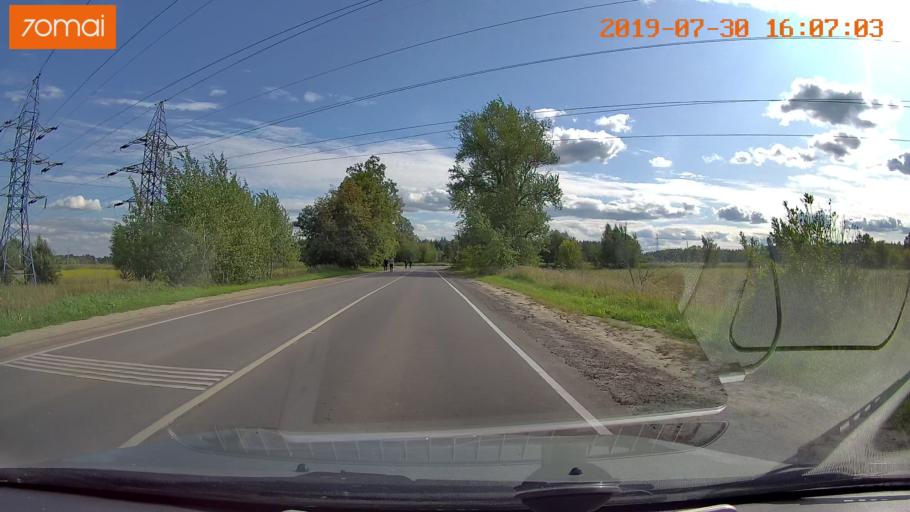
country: RU
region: Moskovskaya
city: Peski
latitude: 55.2505
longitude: 38.7197
